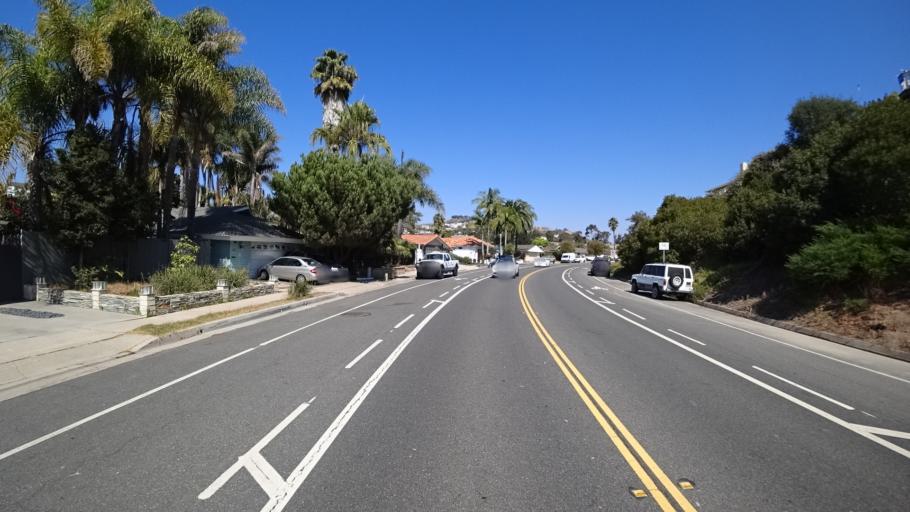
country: US
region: California
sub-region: Orange County
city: San Clemente
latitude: 33.4502
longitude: -117.6456
